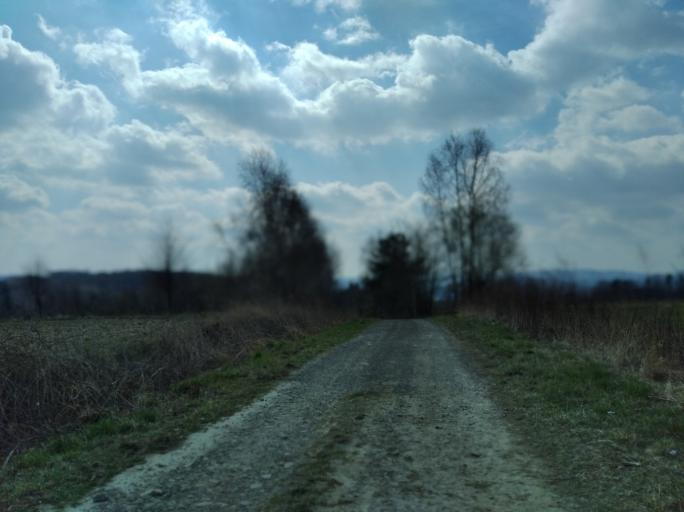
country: PL
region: Subcarpathian Voivodeship
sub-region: Powiat strzyzowski
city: Jawornik
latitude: 49.8266
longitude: 21.8580
